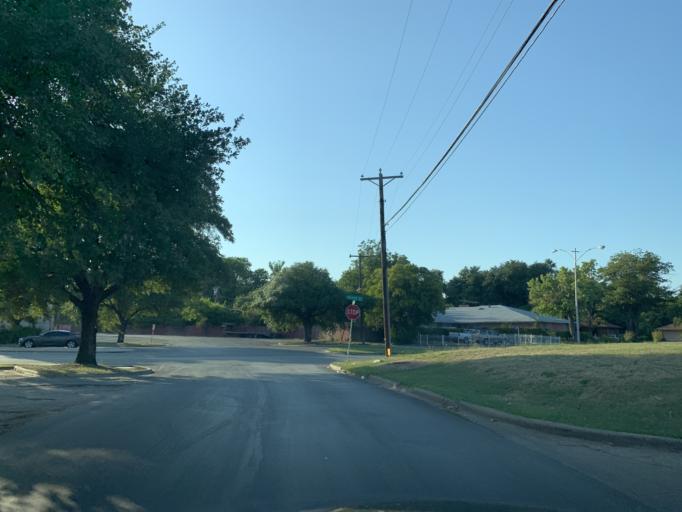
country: US
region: Texas
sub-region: Dallas County
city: Dallas
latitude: 32.7108
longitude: -96.7996
